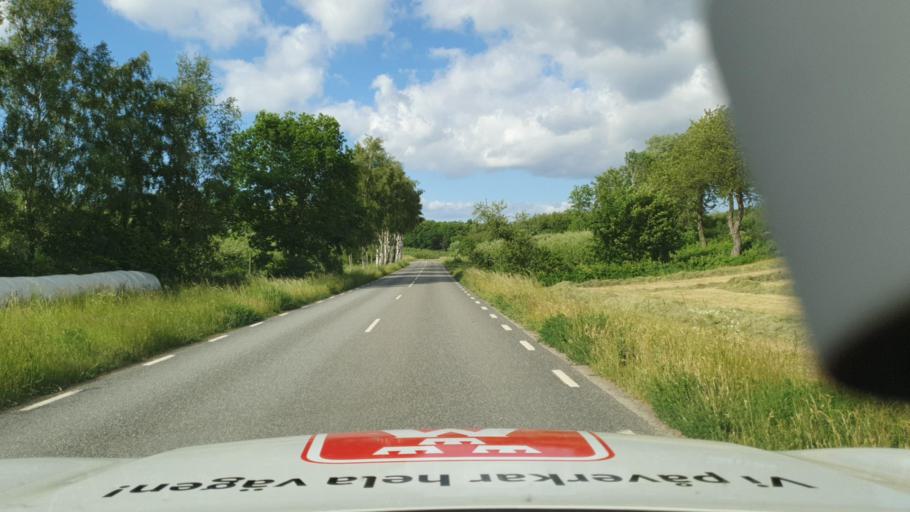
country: SE
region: Skane
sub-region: Simrishamns Kommun
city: Kivik
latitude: 55.6121
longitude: 14.2253
